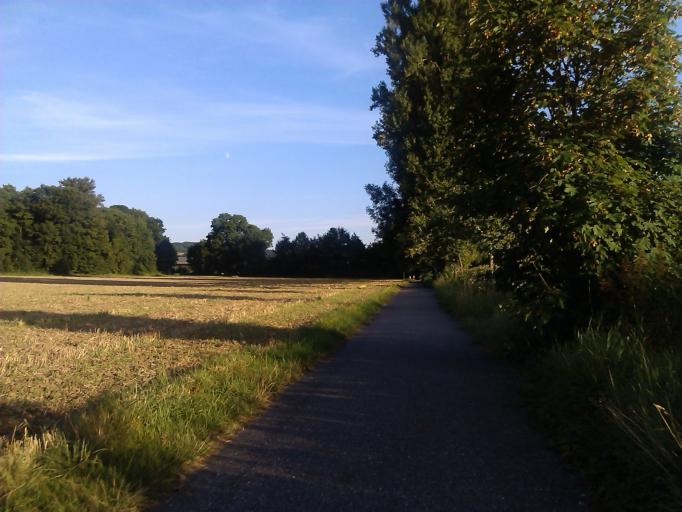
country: DE
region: Baden-Wuerttemberg
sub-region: Karlsruhe Region
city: Rauenberg
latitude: 49.2798
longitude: 8.6957
